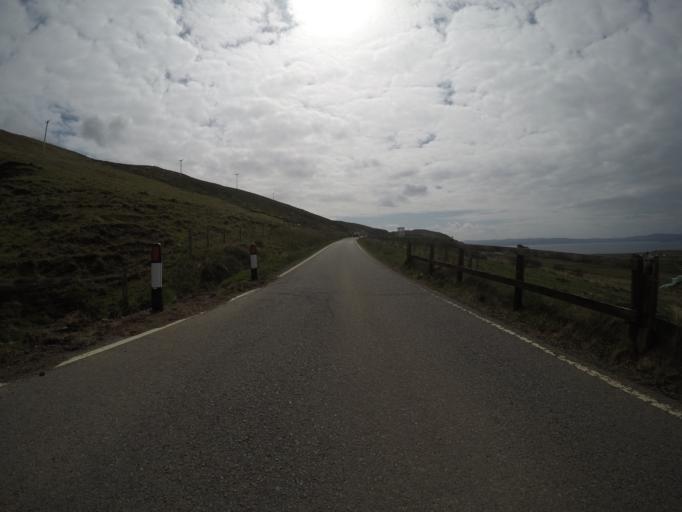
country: GB
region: Scotland
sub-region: Highland
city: Portree
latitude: 57.6083
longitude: -6.3740
